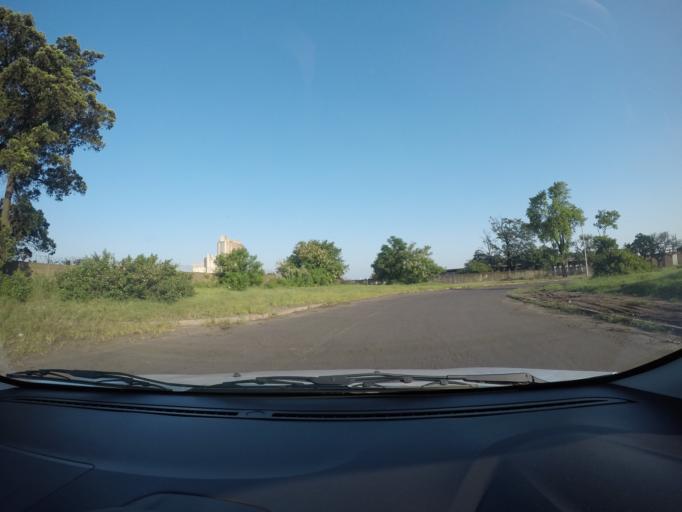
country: ZA
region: KwaZulu-Natal
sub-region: uThungulu District Municipality
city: Richards Bay
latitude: -28.7576
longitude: 32.0100
